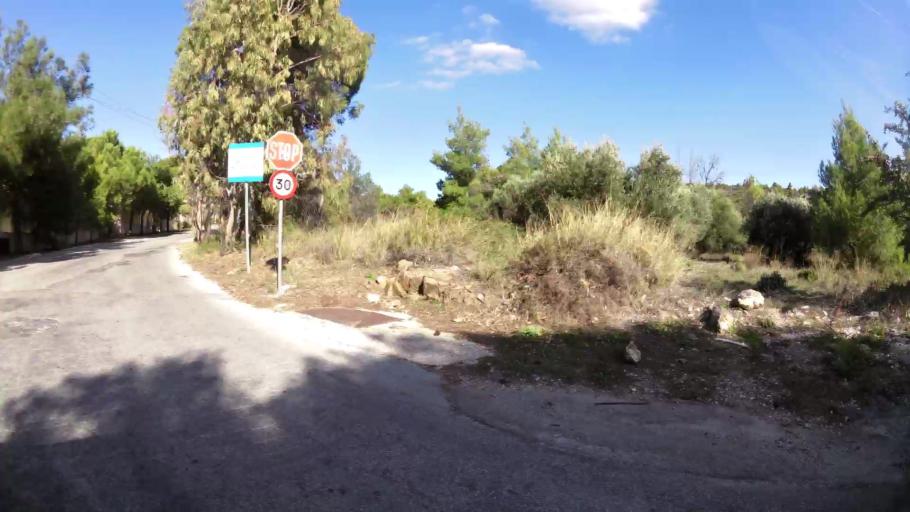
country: GR
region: Attica
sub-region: Nomarchia Anatolikis Attikis
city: Anthousa
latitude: 38.0413
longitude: 23.8826
